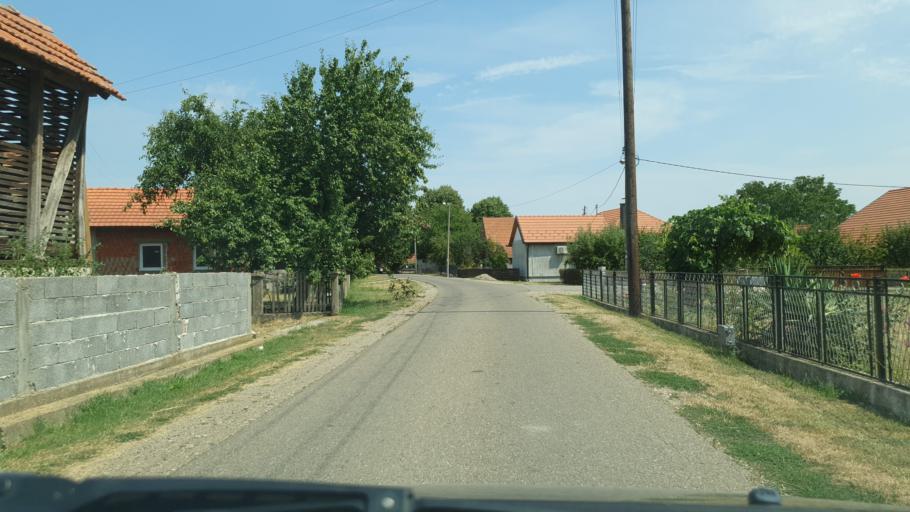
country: BA
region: Republika Srpska
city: Bijeljina
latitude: 44.7247
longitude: 19.2047
